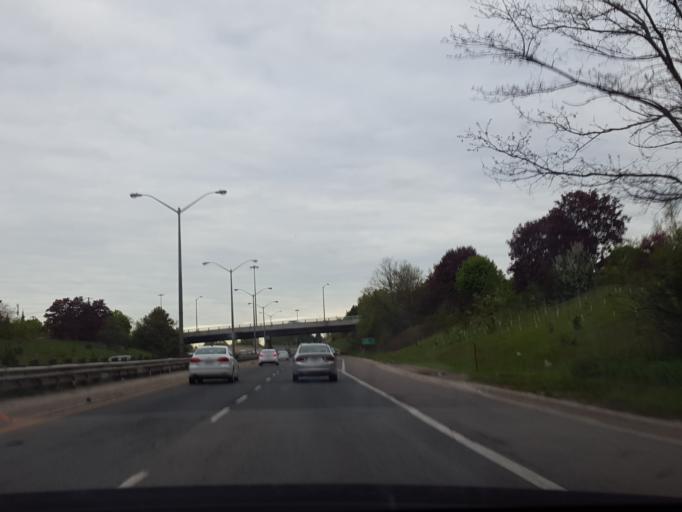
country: CA
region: Ontario
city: Toronto
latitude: 43.7087
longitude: -79.4993
